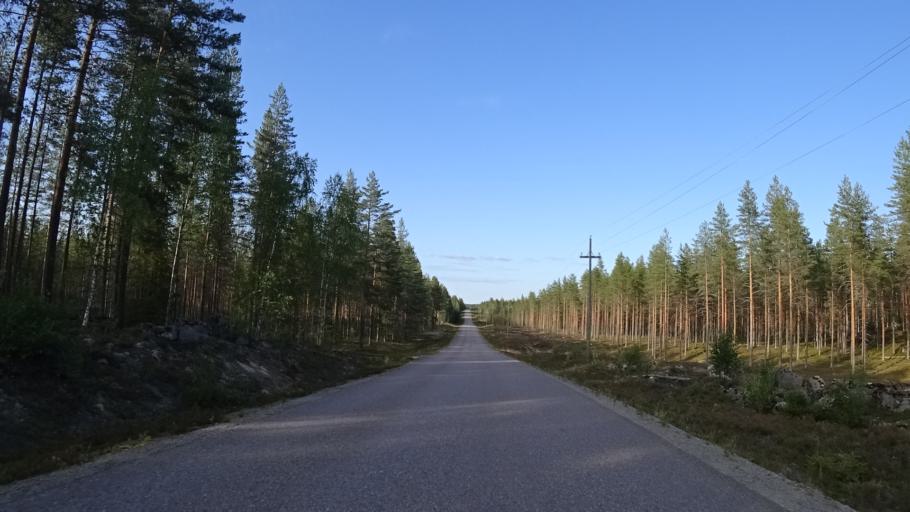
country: FI
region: North Karelia
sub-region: Joensuu
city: Eno
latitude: 63.0656
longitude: 30.5589
